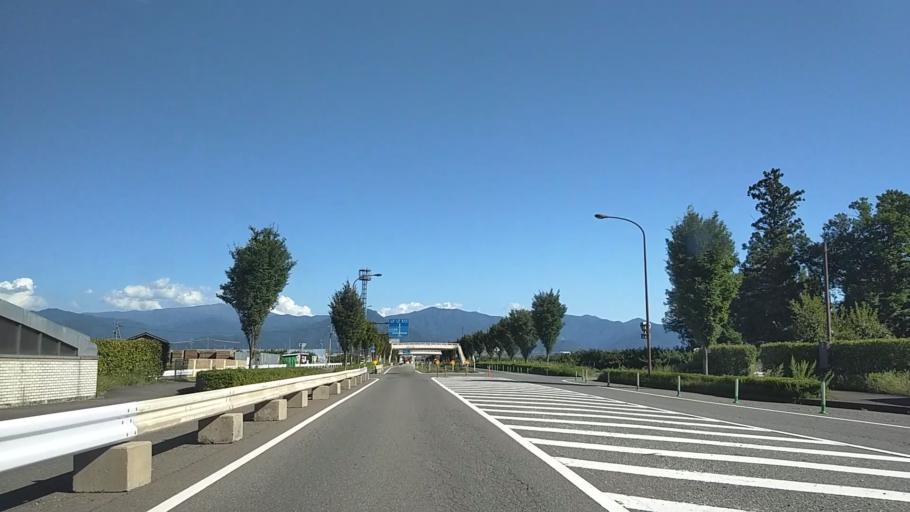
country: JP
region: Nagano
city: Nagano-shi
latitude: 36.6135
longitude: 138.1402
